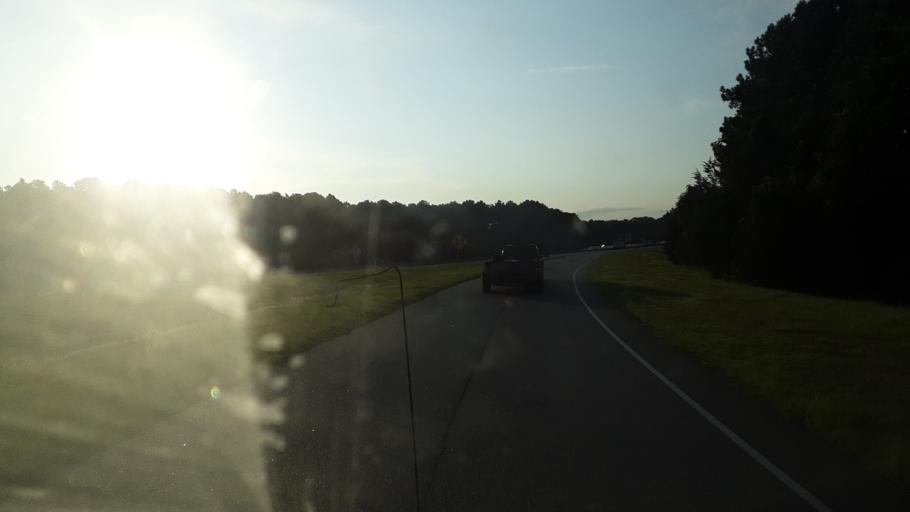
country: US
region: South Carolina
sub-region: Beaufort County
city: Bluffton
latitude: 32.2918
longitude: -80.9352
